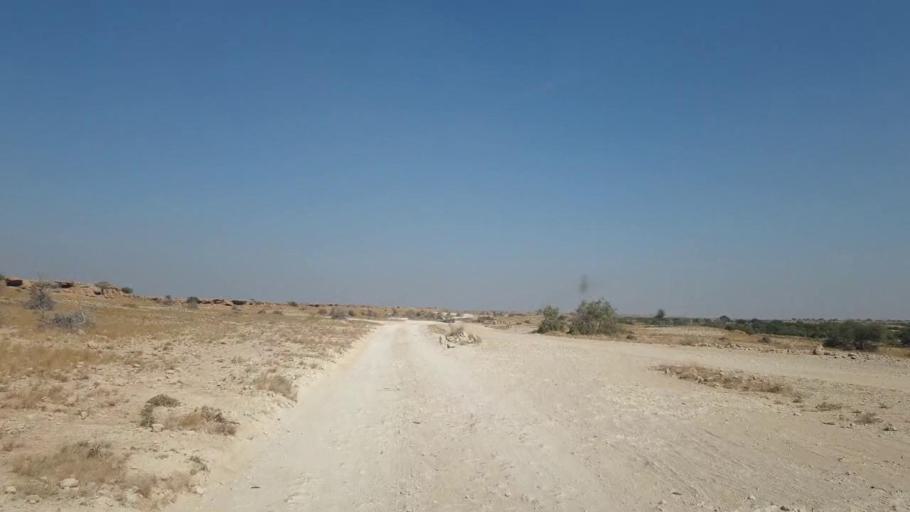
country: PK
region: Sindh
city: Thatta
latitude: 25.2220
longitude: 67.8001
